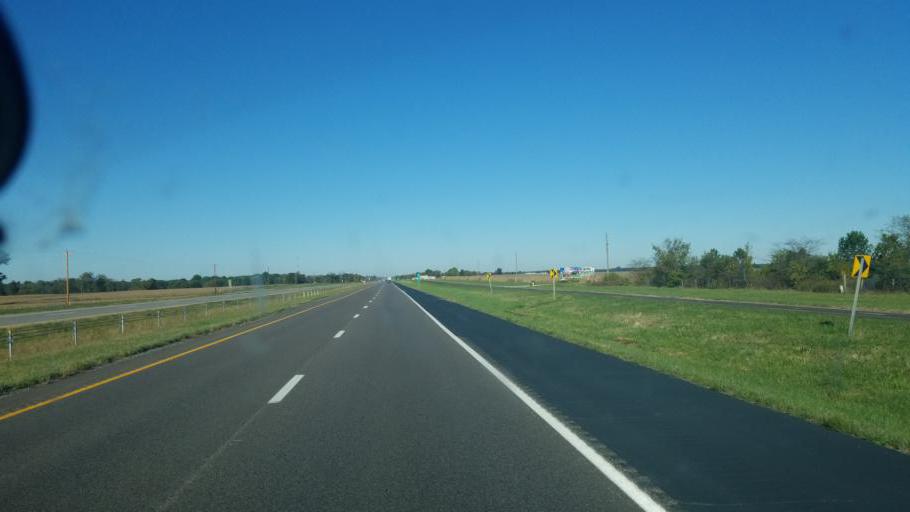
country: US
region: Missouri
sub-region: Callaway County
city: Fulton
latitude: 38.9187
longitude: -91.7497
